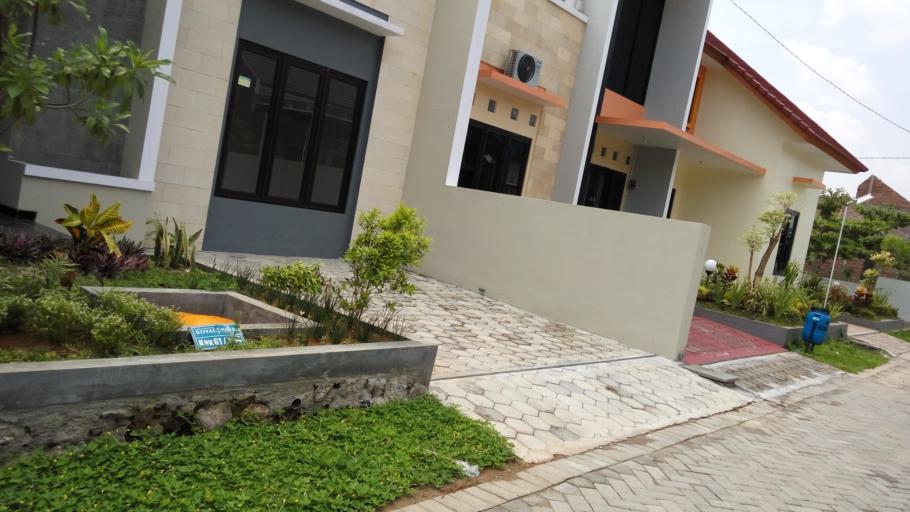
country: ID
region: Central Java
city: Mranggen
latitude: -7.0418
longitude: 110.4801
